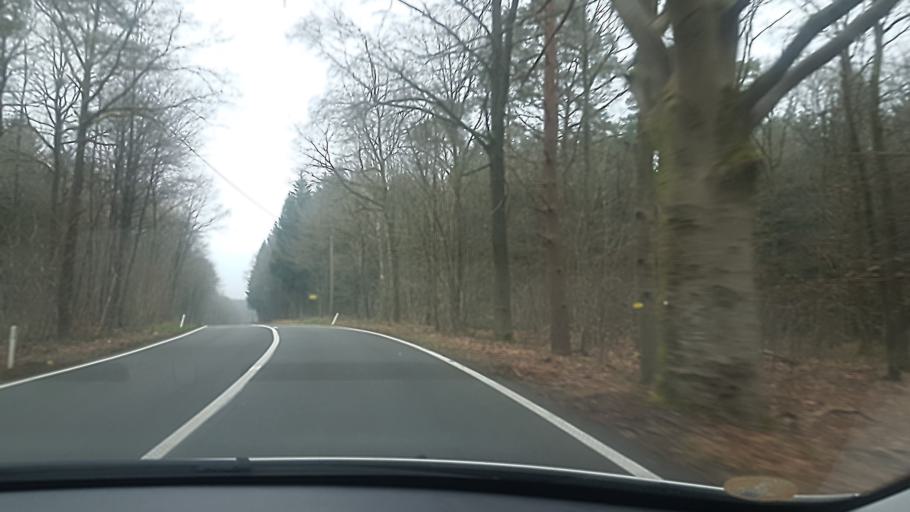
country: FR
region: Champagne-Ardenne
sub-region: Departement des Ardennes
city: Haybes
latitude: 50.0485
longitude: 4.6094
